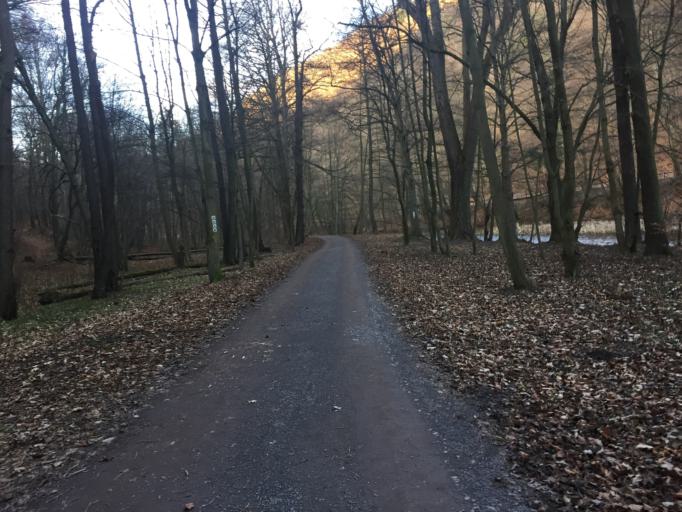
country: DE
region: Thuringia
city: Bad Blankenburg
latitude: 50.6718
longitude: 11.2610
